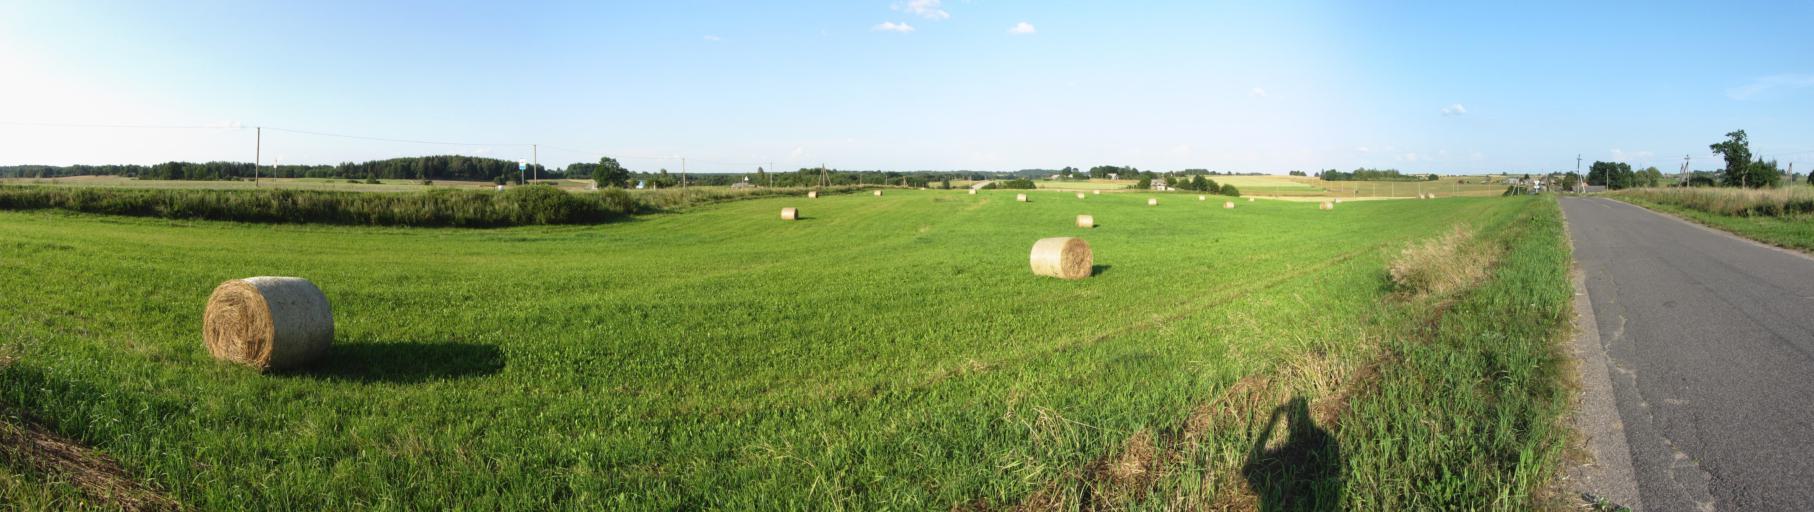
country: LT
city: Dukstas
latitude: 55.3482
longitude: 26.3836
